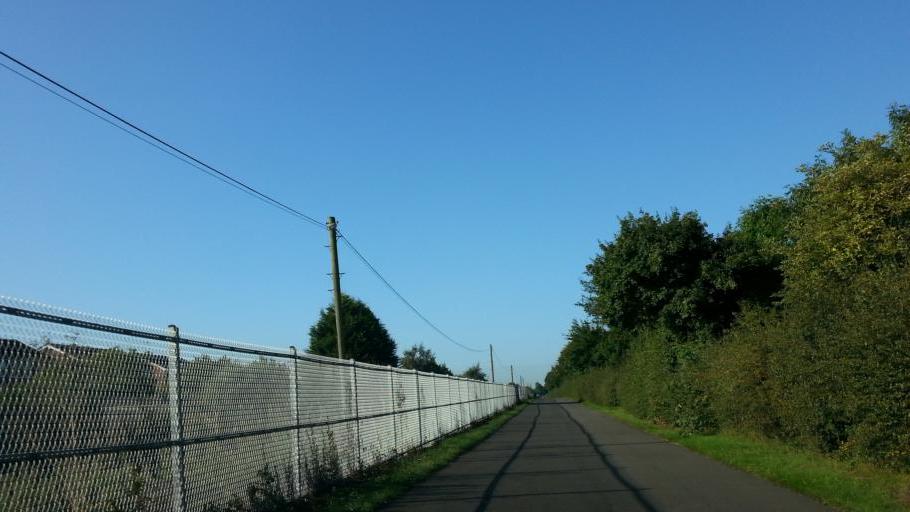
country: GB
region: England
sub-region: Leicestershire
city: Queniborough
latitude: 52.7193
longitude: -1.0559
